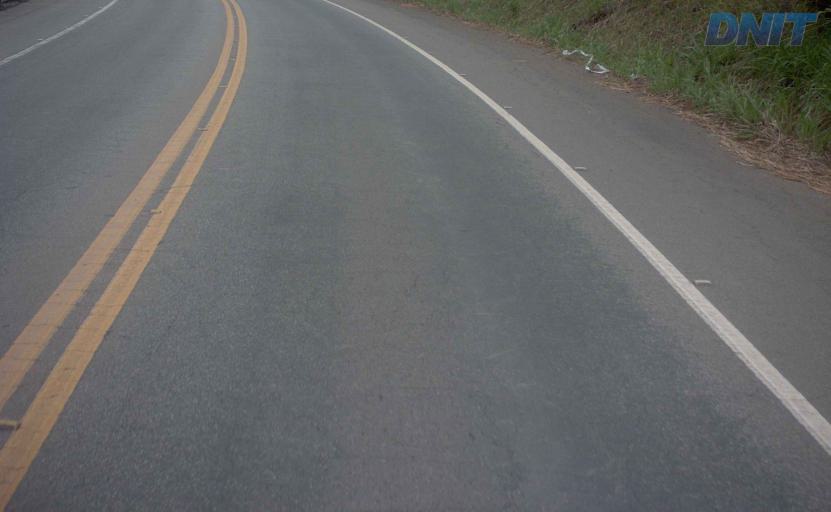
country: BR
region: Minas Gerais
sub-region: Coronel Fabriciano
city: Coronel Fabriciano
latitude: -19.5216
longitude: -42.5815
